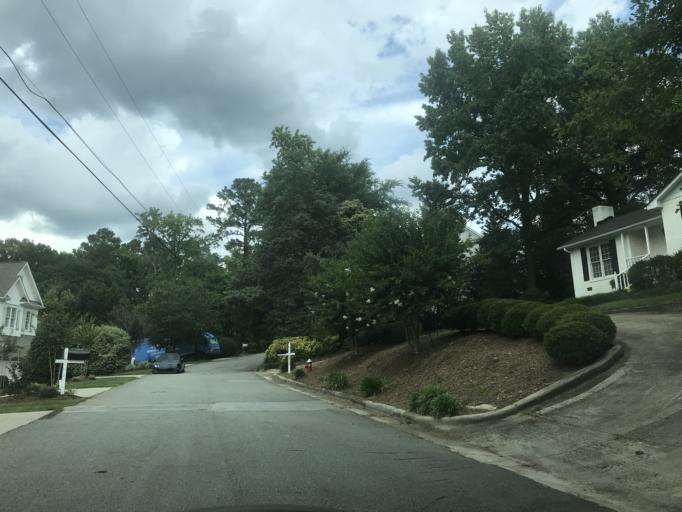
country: US
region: North Carolina
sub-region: Wake County
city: West Raleigh
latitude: 35.8289
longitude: -78.6397
